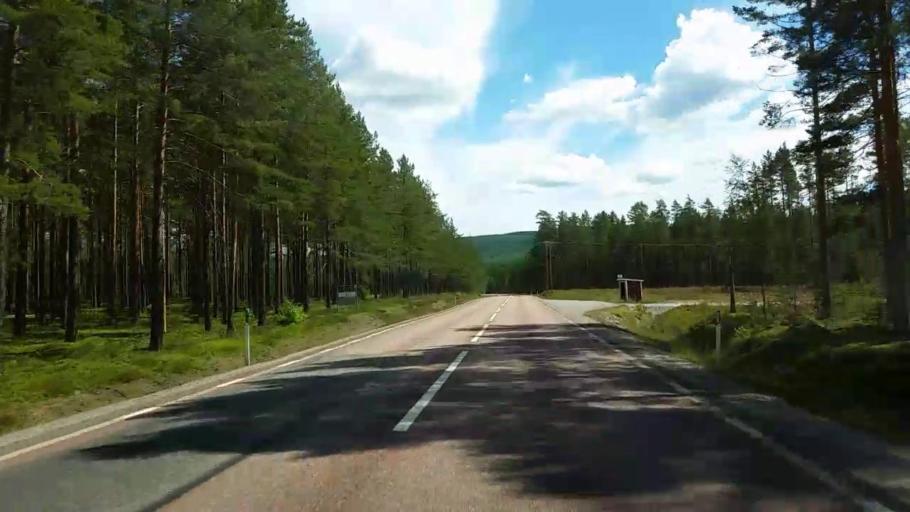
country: SE
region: Gaevleborg
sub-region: Ovanakers Kommun
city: Edsbyn
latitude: 61.3501
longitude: 15.5895
